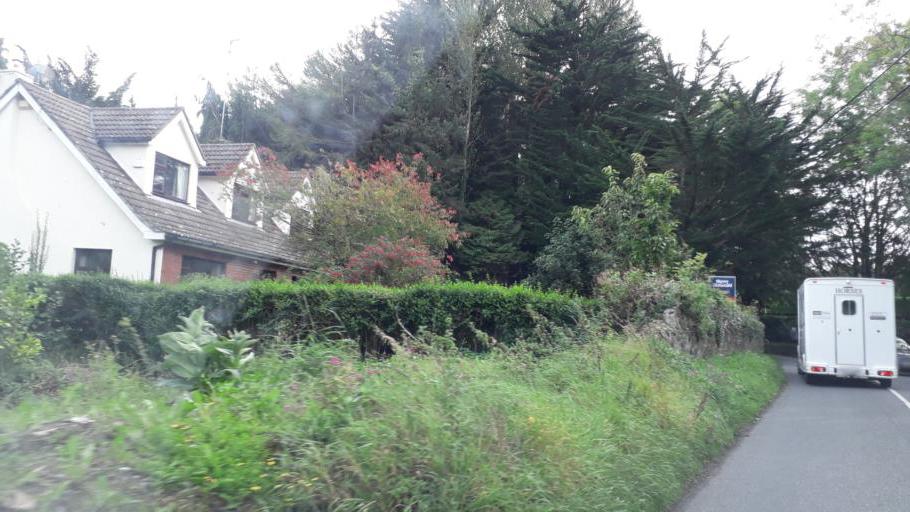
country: IE
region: Leinster
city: Foxrock
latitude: 53.2342
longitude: -6.2001
